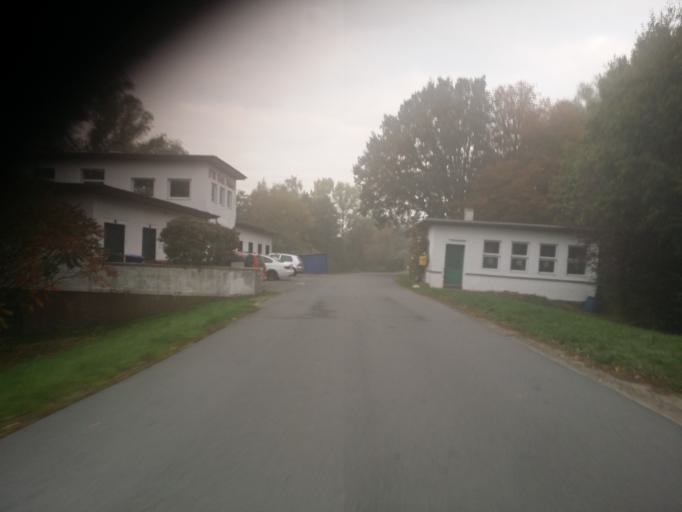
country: DE
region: Lower Saxony
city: Lilienthal
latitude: 53.1308
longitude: 8.8630
